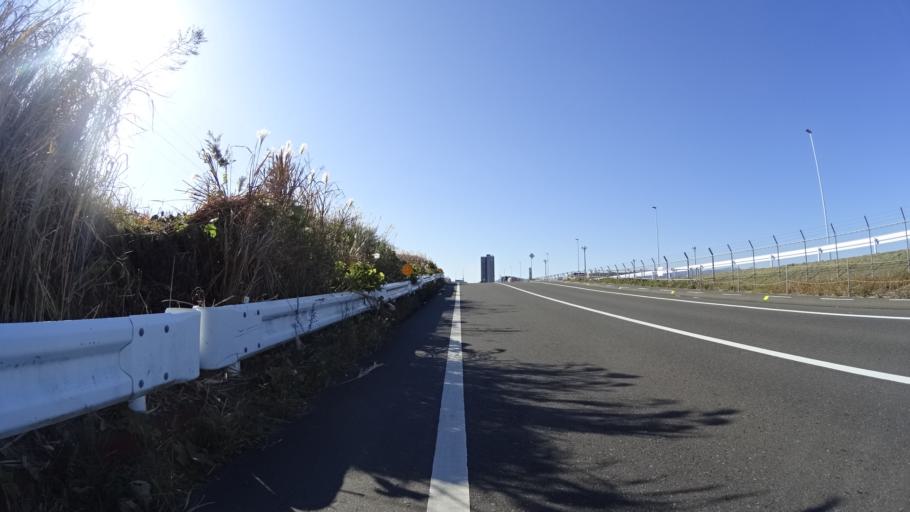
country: JP
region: Tokyo
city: Hachioji
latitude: 35.5875
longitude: 139.3770
